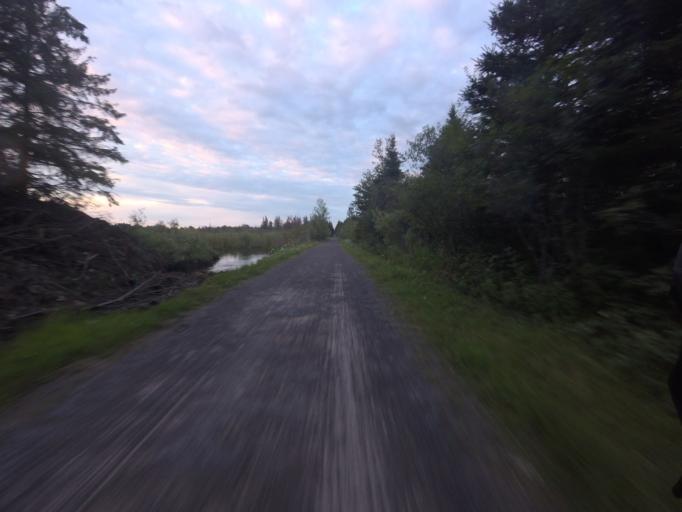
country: CA
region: Ontario
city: Bells Corners
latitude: 45.2335
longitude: -75.9600
